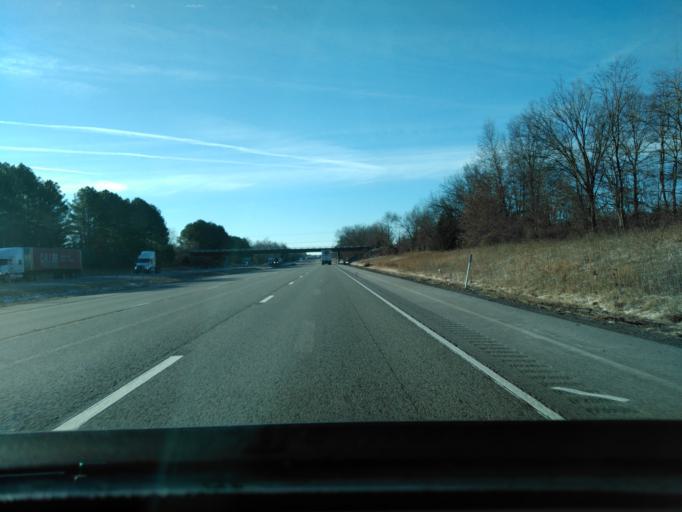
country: US
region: Illinois
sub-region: Williamson County
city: Johnston City
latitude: 37.7943
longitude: -88.9461
